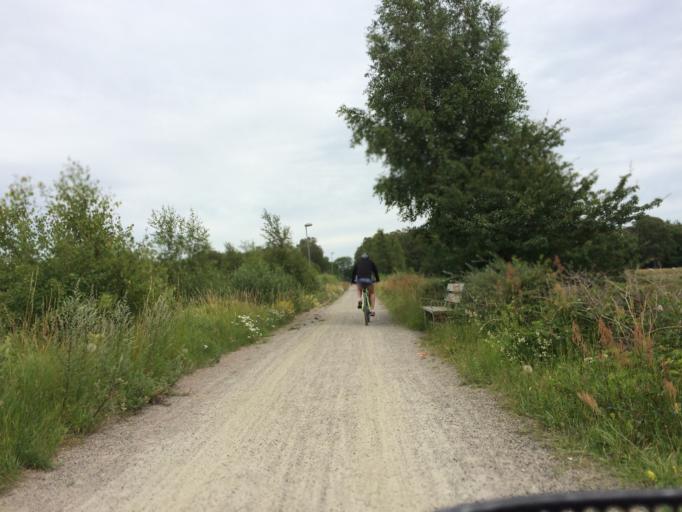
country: SE
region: Skane
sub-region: Vellinge Kommun
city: Ljunghusen
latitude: 55.4064
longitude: 12.9057
